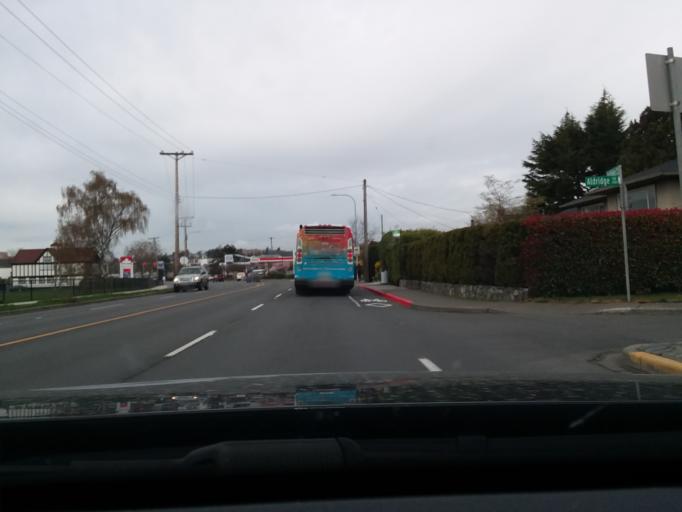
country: CA
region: British Columbia
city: Oak Bay
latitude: 48.4462
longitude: -123.3307
